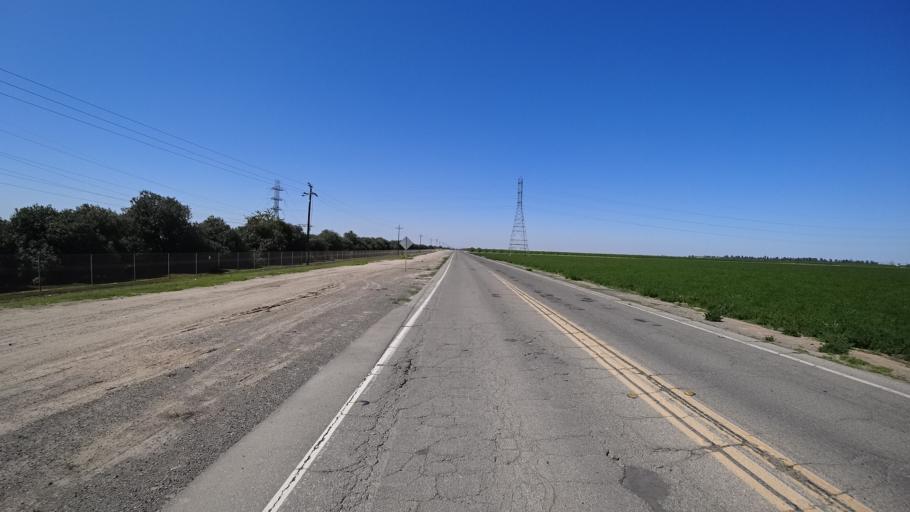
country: US
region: California
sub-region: Fresno County
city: West Park
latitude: 36.7063
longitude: -119.8950
